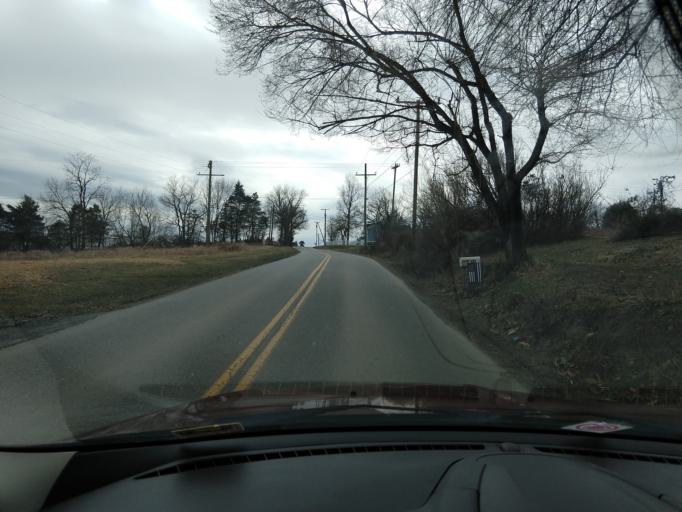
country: US
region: Virginia
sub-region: Augusta County
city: Crimora
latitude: 38.1925
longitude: -78.9103
